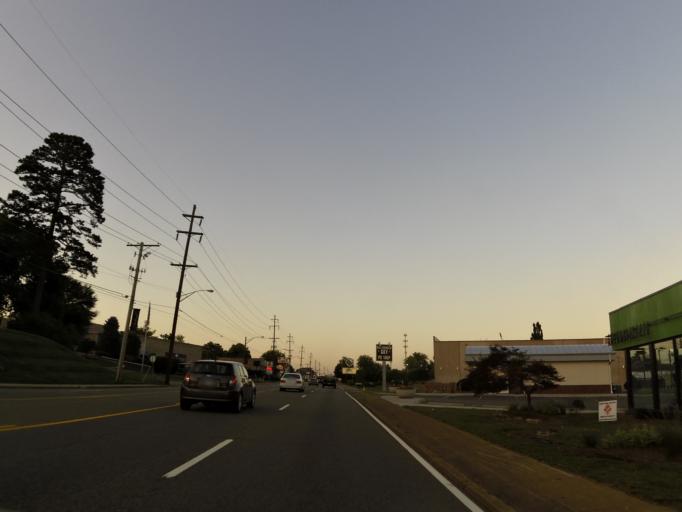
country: US
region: Tennessee
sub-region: Knox County
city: Knoxville
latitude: 35.9363
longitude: -83.9919
